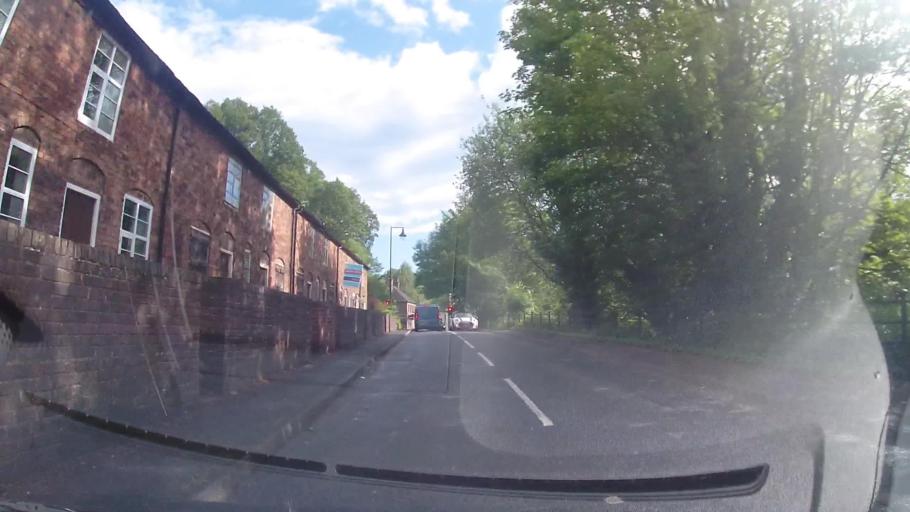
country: GB
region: England
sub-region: Telford and Wrekin
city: Ironbridge
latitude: 52.6402
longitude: -2.4916
